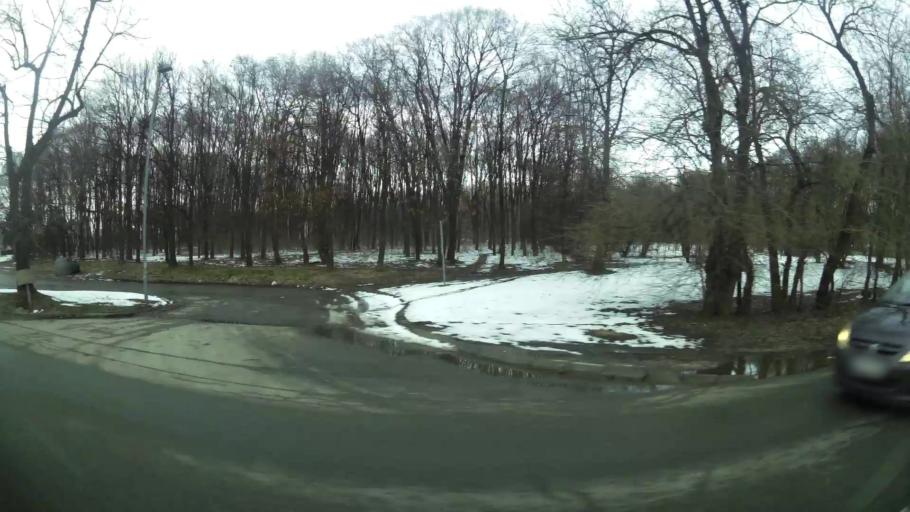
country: RS
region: Central Serbia
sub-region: Belgrade
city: Rakovica
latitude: 44.7302
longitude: 20.4837
